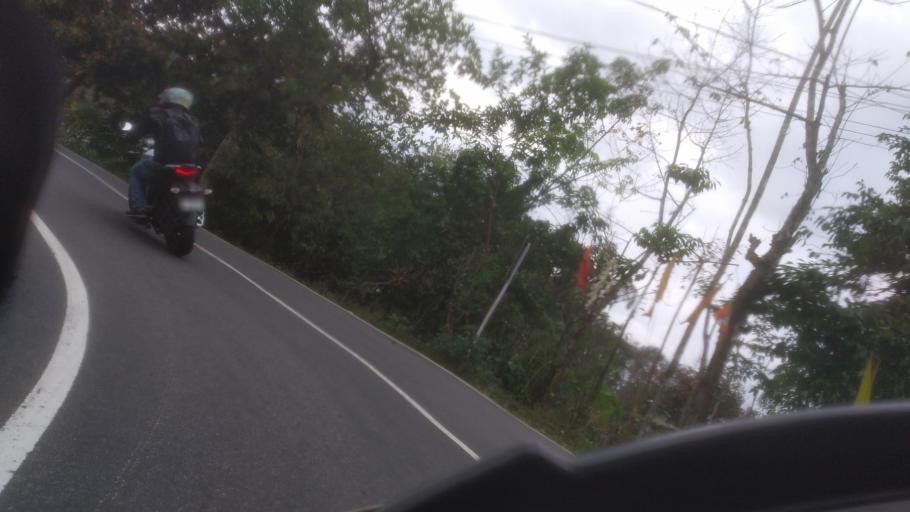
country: IN
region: Kerala
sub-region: Idukki
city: Idukki
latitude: 9.9642
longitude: 77.0004
